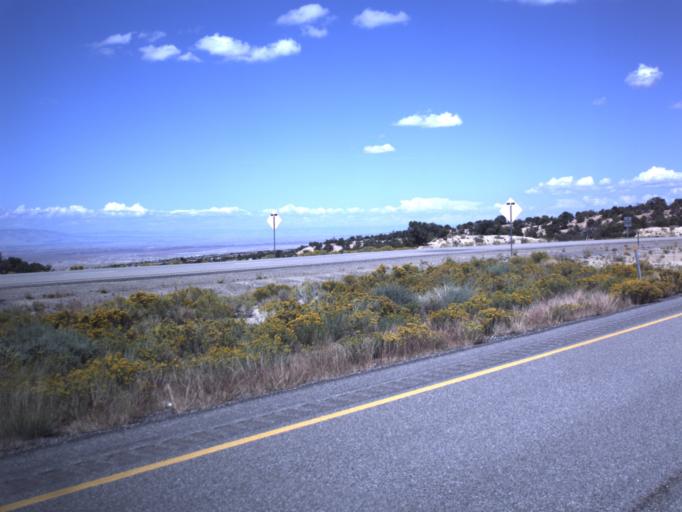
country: US
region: Utah
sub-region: Emery County
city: Ferron
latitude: 38.8515
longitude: -110.9263
